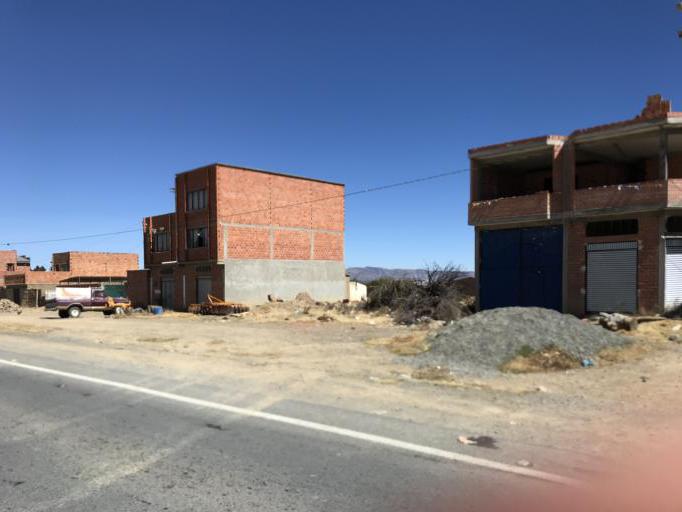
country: BO
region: La Paz
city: Huarina
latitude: -16.2039
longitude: -68.5961
